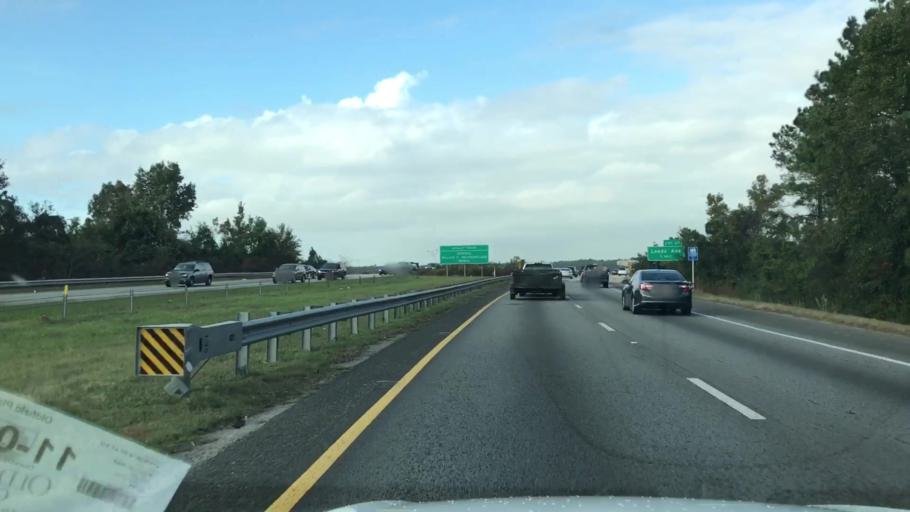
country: US
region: South Carolina
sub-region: Charleston County
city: North Charleston
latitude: 32.8278
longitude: -80.0297
